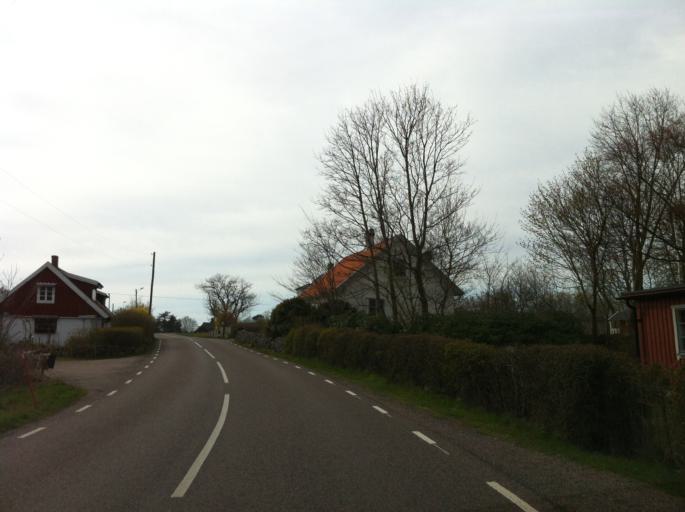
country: SE
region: Skane
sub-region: Hoganas Kommun
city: Hoganas
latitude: 56.2599
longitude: 12.6039
